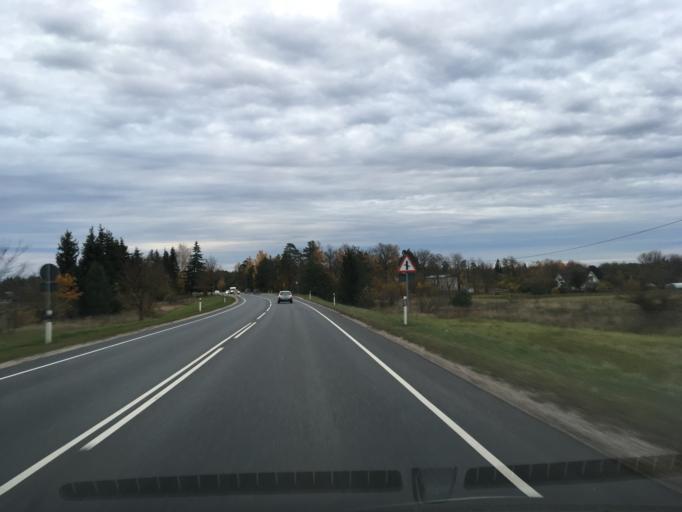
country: EE
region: Harju
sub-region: Nissi vald
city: Turba
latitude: 59.0985
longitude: 24.2514
